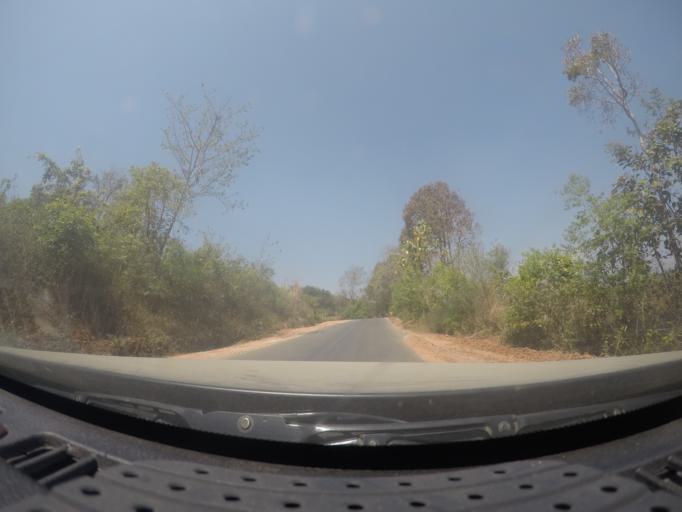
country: MM
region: Shan
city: Taunggyi
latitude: 20.9756
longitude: 96.5411
